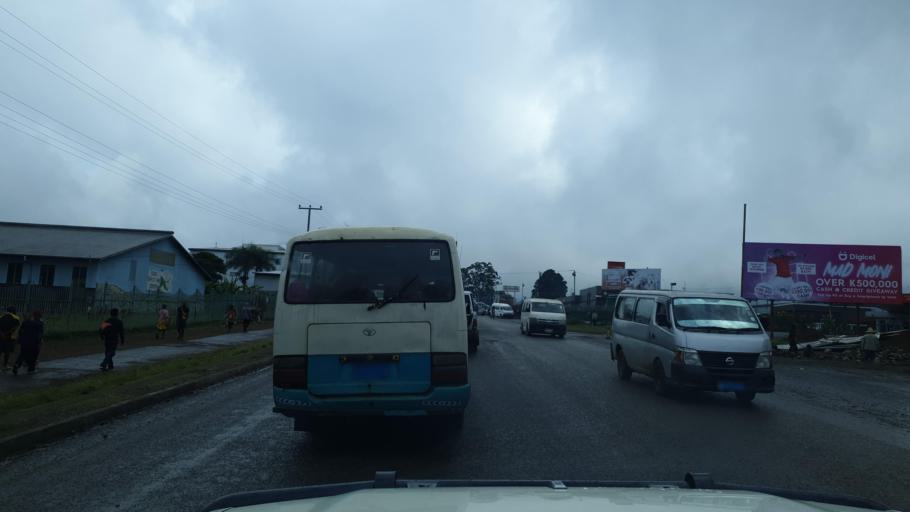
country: PG
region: Eastern Highlands
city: Goroka
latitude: -6.0751
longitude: 145.3891
